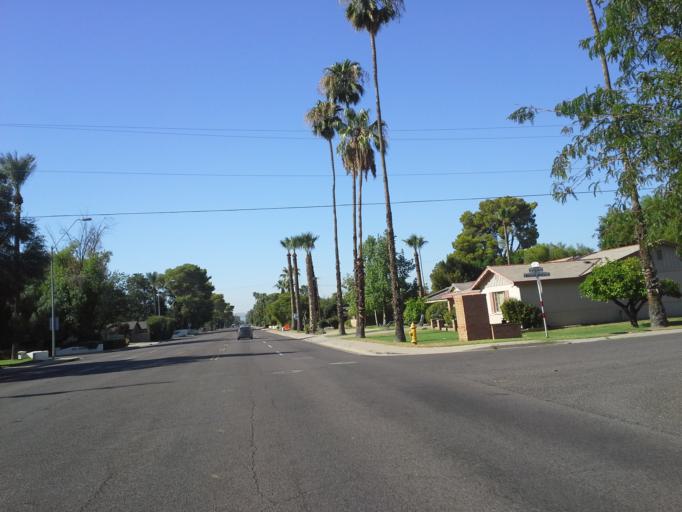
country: US
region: Arizona
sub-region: Maricopa County
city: Phoenix
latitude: 33.5468
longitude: -112.0826
